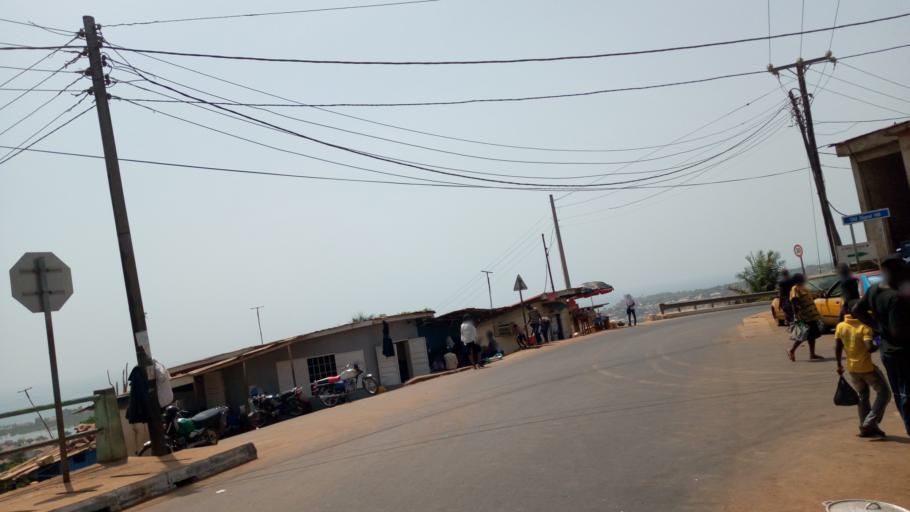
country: SL
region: Western Area
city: Freetown
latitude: 8.4807
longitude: -13.2653
